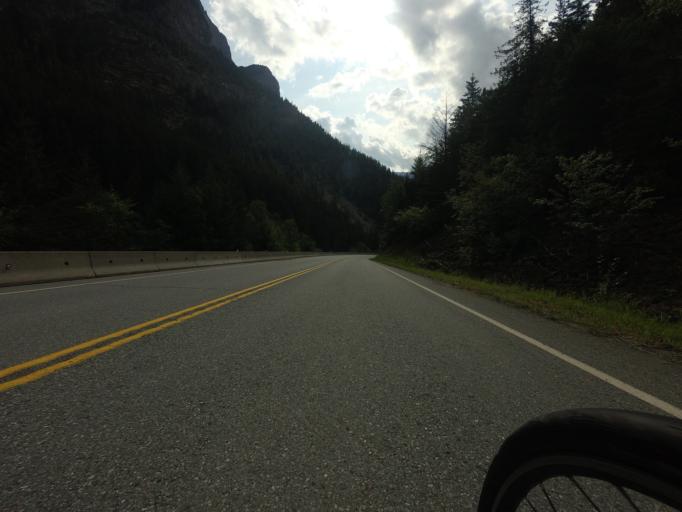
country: CA
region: British Columbia
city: Lillooet
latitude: 50.6447
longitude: -122.0596
